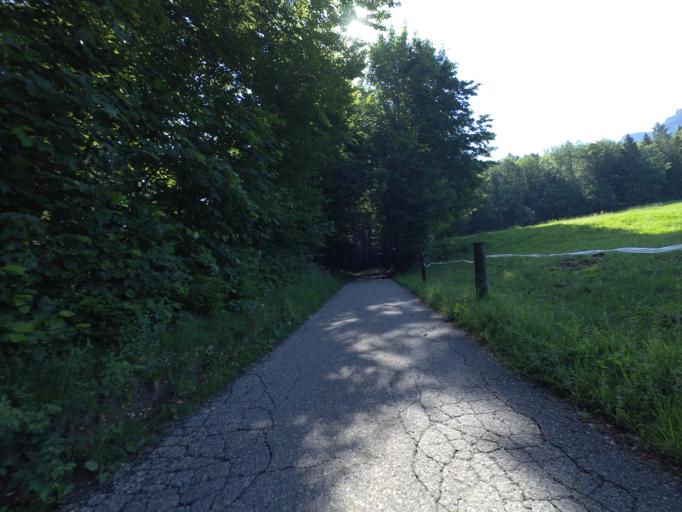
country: DE
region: Bavaria
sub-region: Upper Bavaria
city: Piding
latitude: 47.7371
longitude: 12.9382
